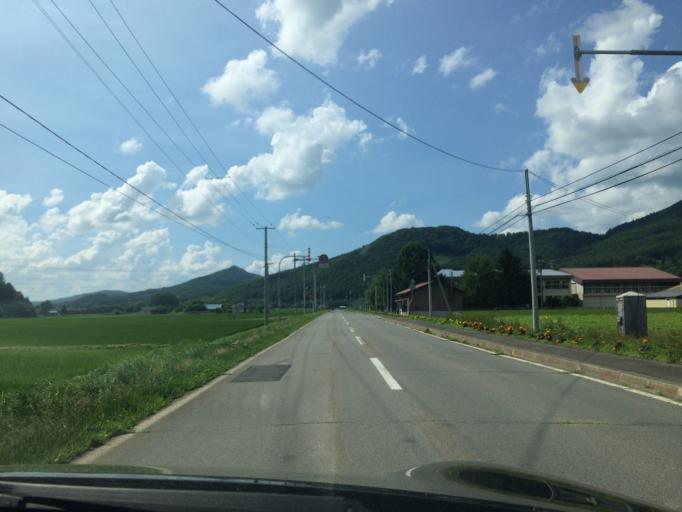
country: JP
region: Hokkaido
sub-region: Asahikawa-shi
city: Asahikawa
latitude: 43.7536
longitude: 142.5492
